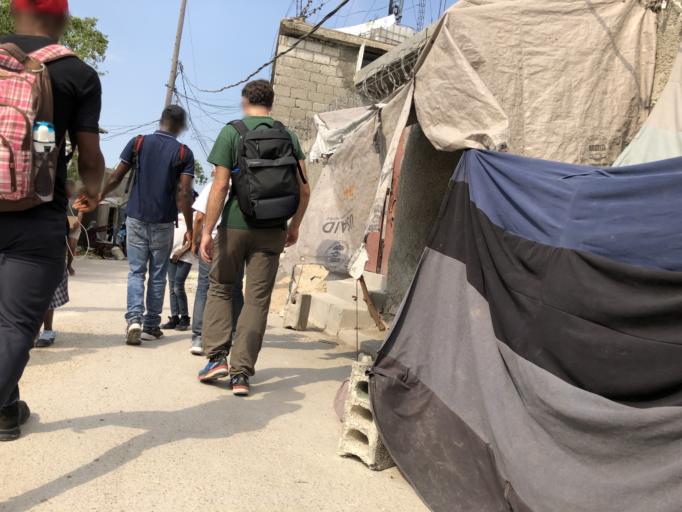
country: HT
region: Ouest
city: Port-au-Prince
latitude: 18.5237
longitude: -72.3177
